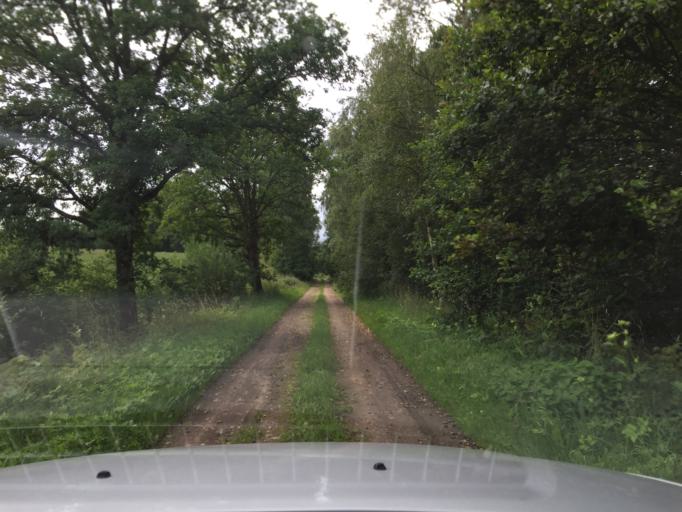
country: SE
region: Skane
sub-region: Hassleholms Kommun
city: Sosdala
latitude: 56.0325
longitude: 13.6936
